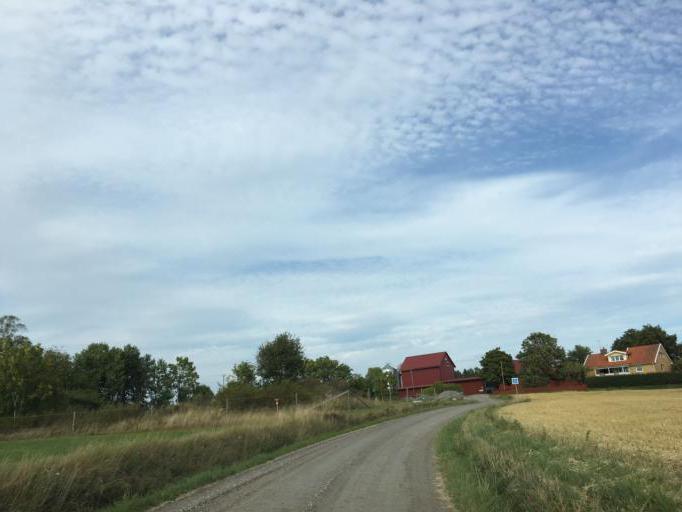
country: SE
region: Soedermanland
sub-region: Eskilstuna Kommun
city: Eskilstuna
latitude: 59.4073
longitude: 16.5098
